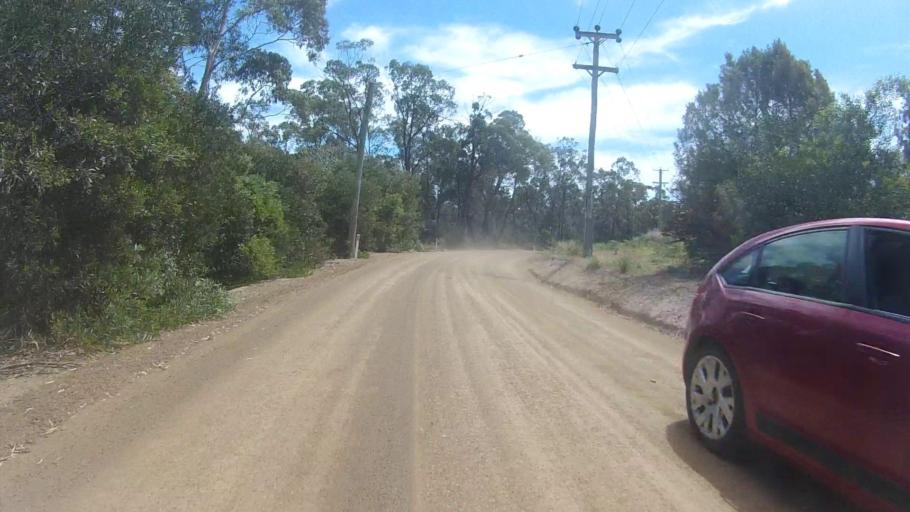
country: AU
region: Tasmania
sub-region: Kingborough
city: Blackmans Bay
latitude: -43.0445
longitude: 147.3060
